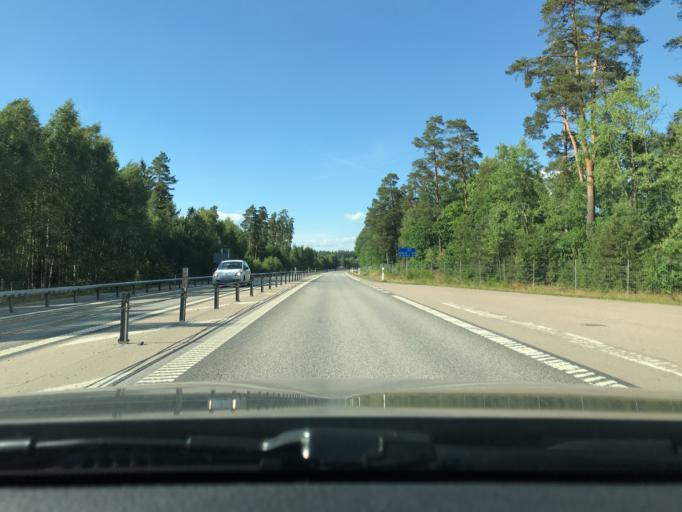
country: SE
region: Skane
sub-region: Osby Kommun
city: Osby
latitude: 56.3964
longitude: 14.0373
